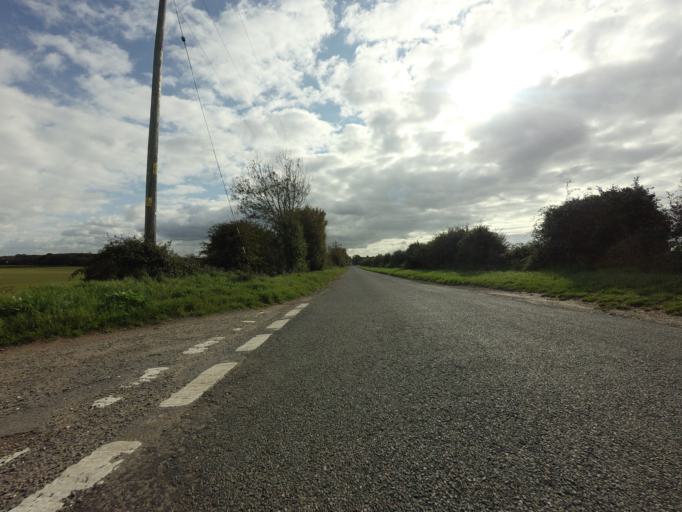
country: GB
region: England
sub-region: Norfolk
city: Heacham
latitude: 52.9113
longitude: 0.5430
